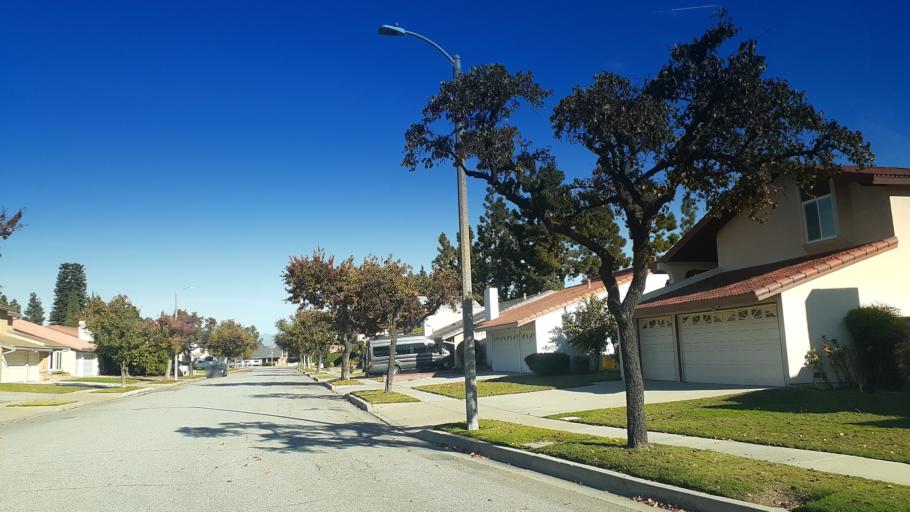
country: US
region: California
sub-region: Los Angeles County
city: Cerritos
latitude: 33.8562
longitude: -118.0655
